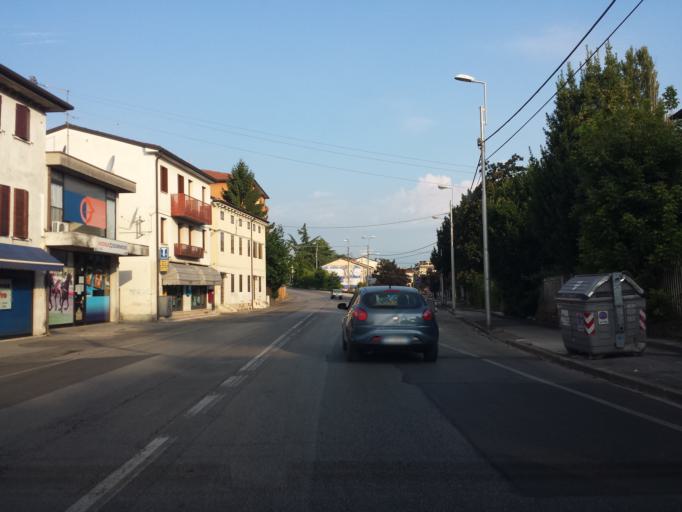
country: IT
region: Veneto
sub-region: Provincia di Vicenza
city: Vicenza
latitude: 45.5436
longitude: 11.5691
